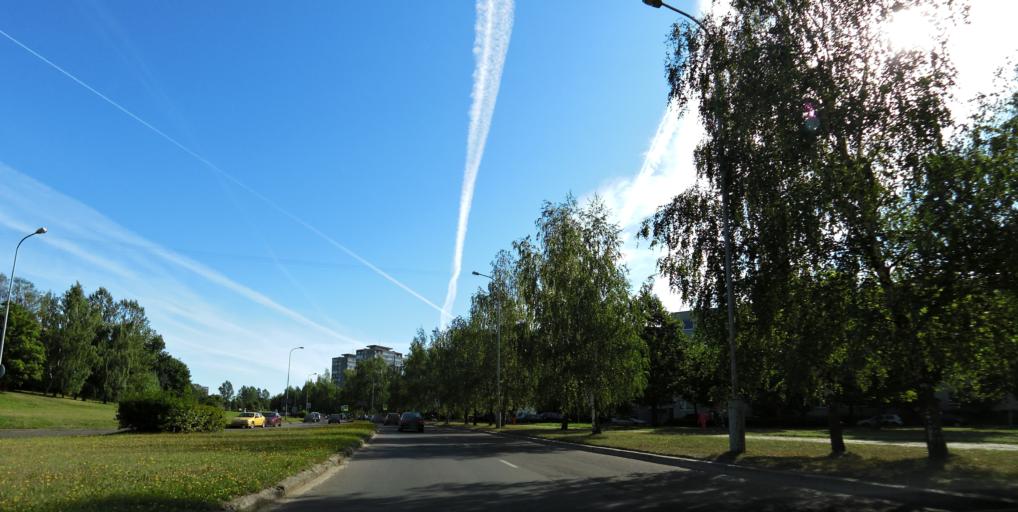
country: LT
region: Vilnius County
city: Justiniskes
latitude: 54.7062
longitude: 25.2166
